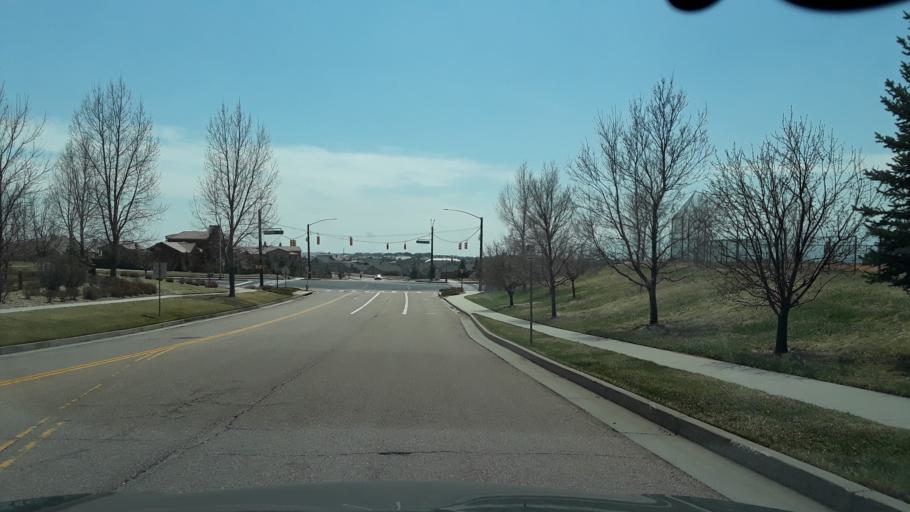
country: US
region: Colorado
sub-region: El Paso County
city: Gleneagle
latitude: 39.0311
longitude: -104.7903
